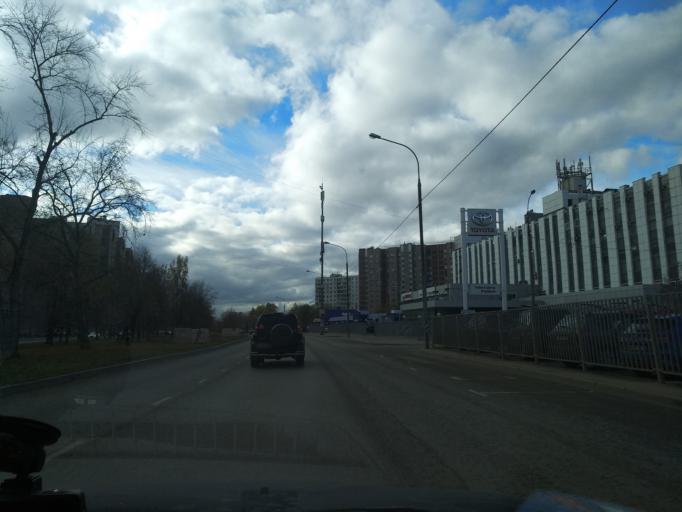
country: RU
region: Moscow
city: Otradnoye
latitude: 55.8719
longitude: 37.5949
